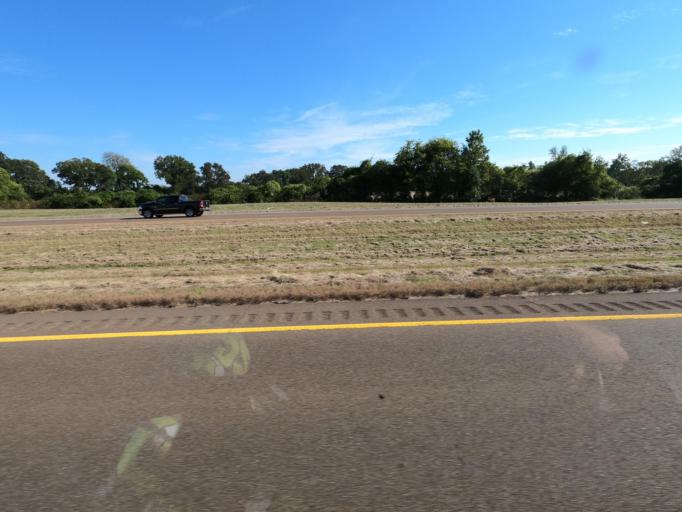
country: US
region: Tennessee
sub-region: Dyer County
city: Dyersburg
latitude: 36.0821
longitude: -89.3347
